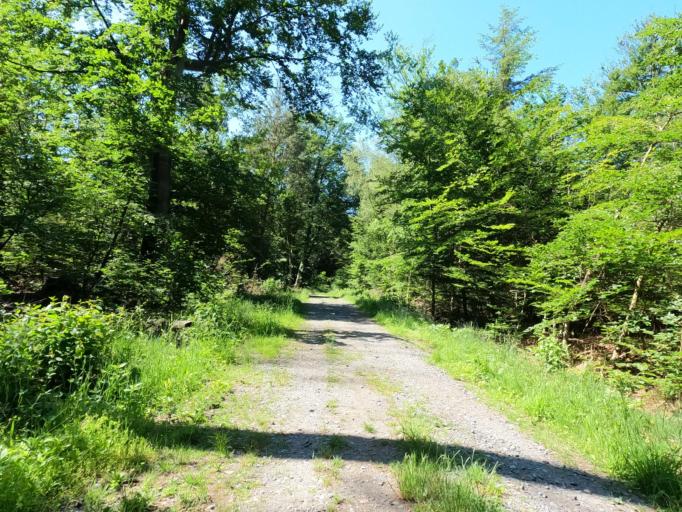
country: DE
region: Hesse
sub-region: Regierungsbezirk Darmstadt
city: Offenbach
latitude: 50.0701
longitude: 8.7377
